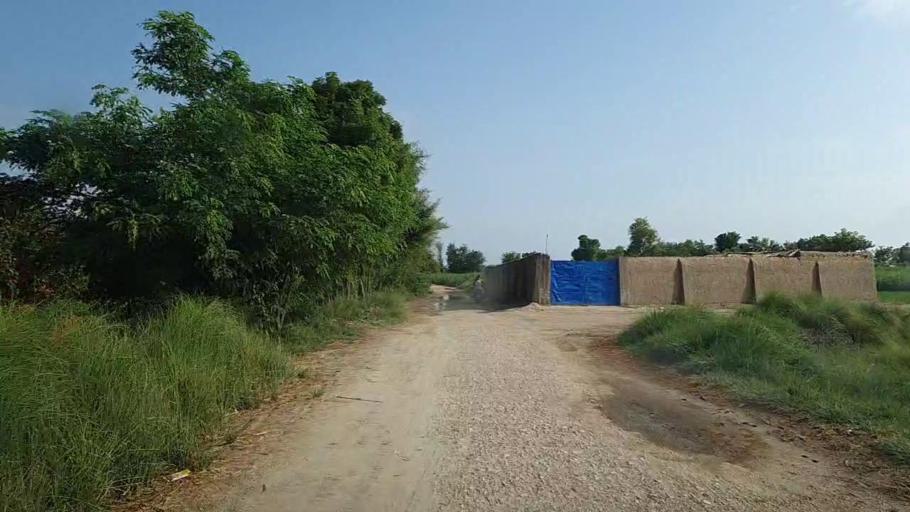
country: PK
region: Sindh
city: Bhiria
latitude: 26.8460
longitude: 68.2398
